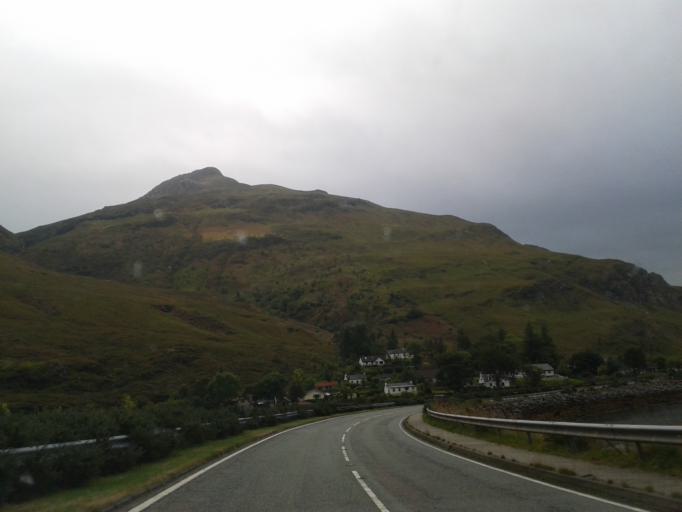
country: GB
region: Scotland
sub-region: Highland
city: Fort William
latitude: 57.2308
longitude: -5.4027
